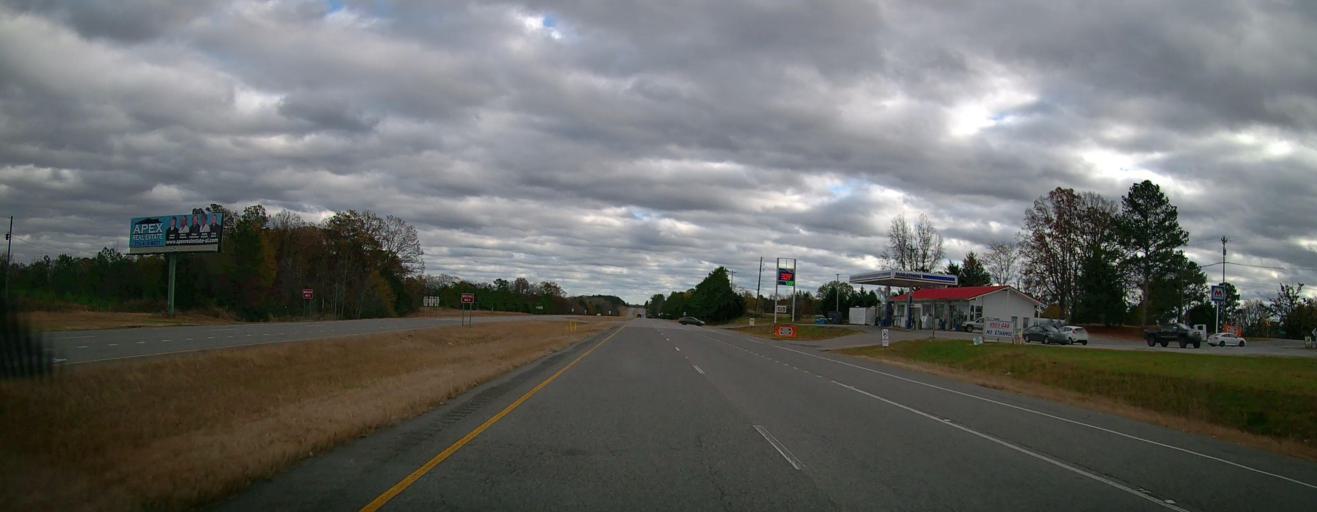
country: US
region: Alabama
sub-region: Lawrence County
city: Town Creek
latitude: 34.5889
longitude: -87.4242
